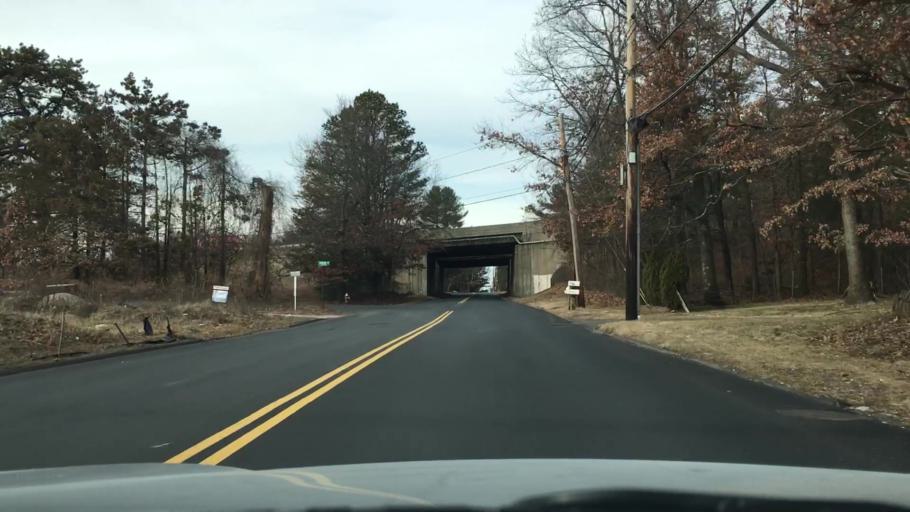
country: US
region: Massachusetts
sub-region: Hampden County
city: Westfield
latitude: 42.1452
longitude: -72.7394
